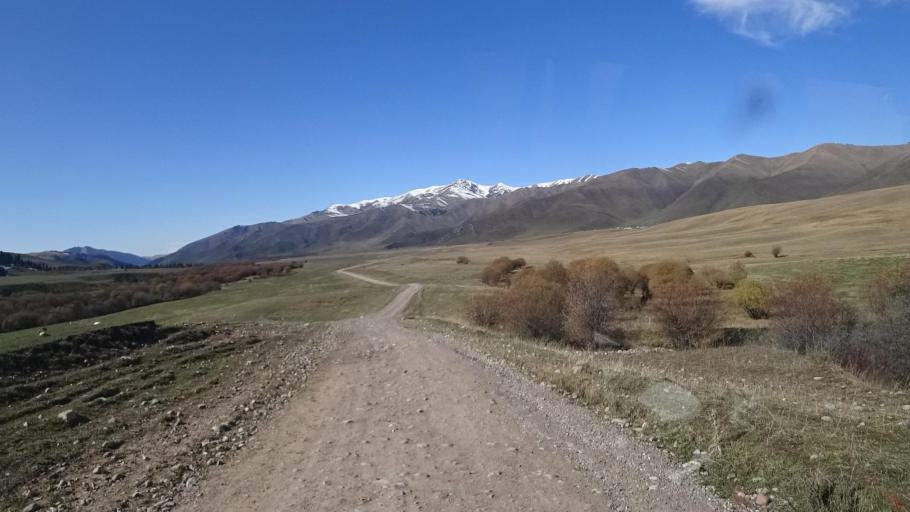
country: KZ
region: Almaty Oblysy
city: Kegen
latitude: 42.7362
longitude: 79.0163
